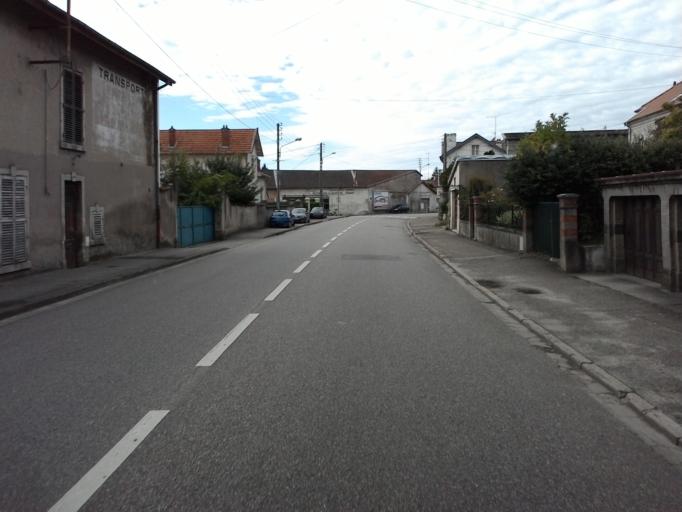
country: FR
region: Lorraine
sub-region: Departement de Meurthe-et-Moselle
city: Toul
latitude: 48.6840
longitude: 5.8962
